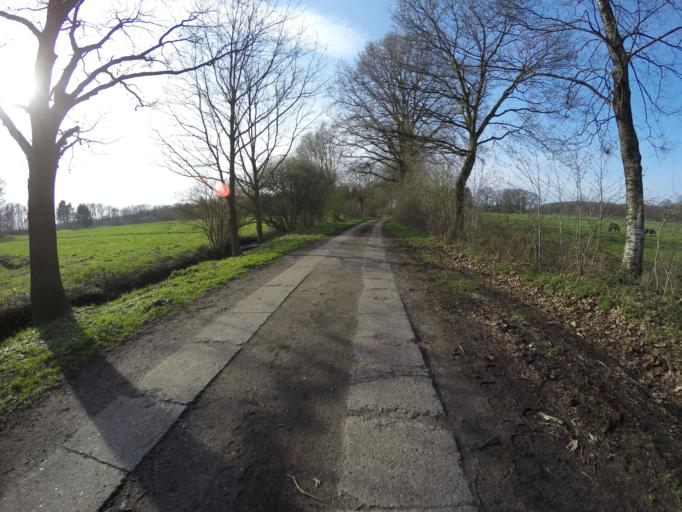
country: DE
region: Schleswig-Holstein
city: Bilsen
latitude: 53.7480
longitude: 9.8729
